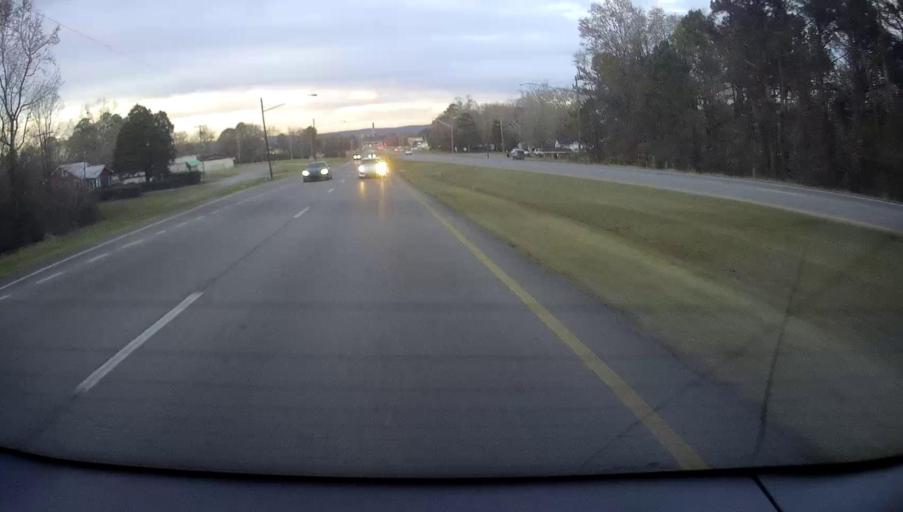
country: US
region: Alabama
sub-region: Etowah County
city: Gadsden
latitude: 33.9912
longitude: -85.9673
